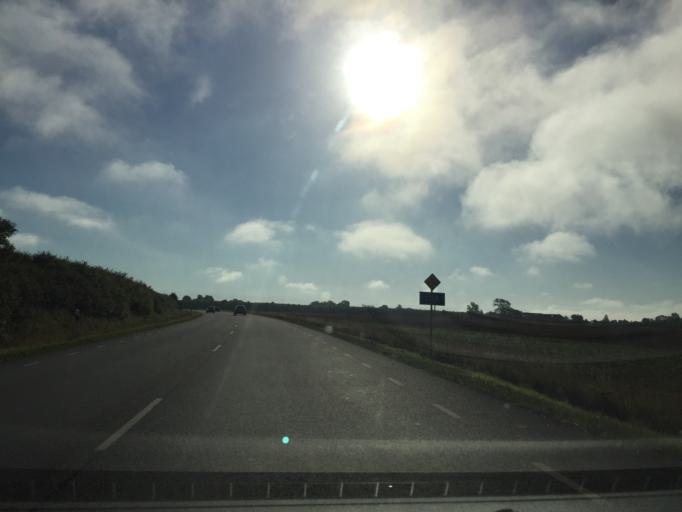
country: SE
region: Skane
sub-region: Staffanstorps Kommun
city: Hjaerup
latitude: 55.6821
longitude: 13.1637
